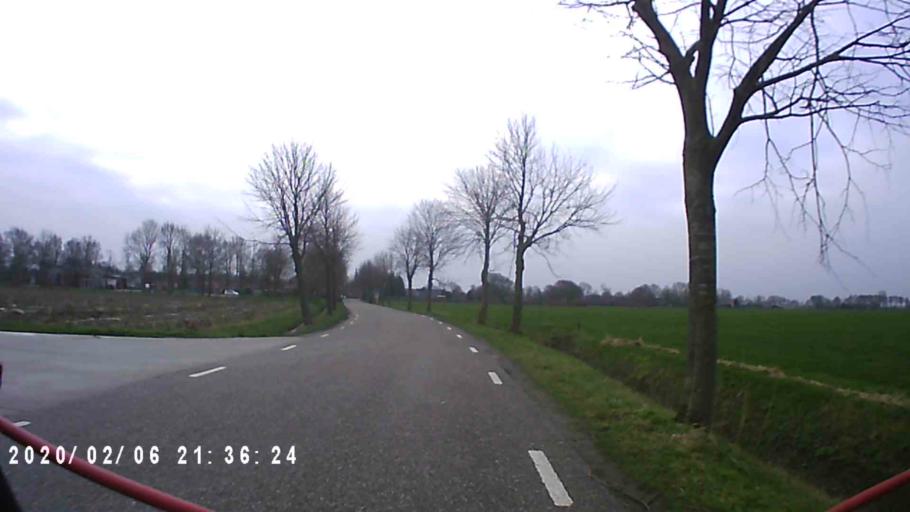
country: NL
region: Groningen
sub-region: Gemeente Zuidhorn
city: Noordhorn
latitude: 53.2674
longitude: 6.3941
